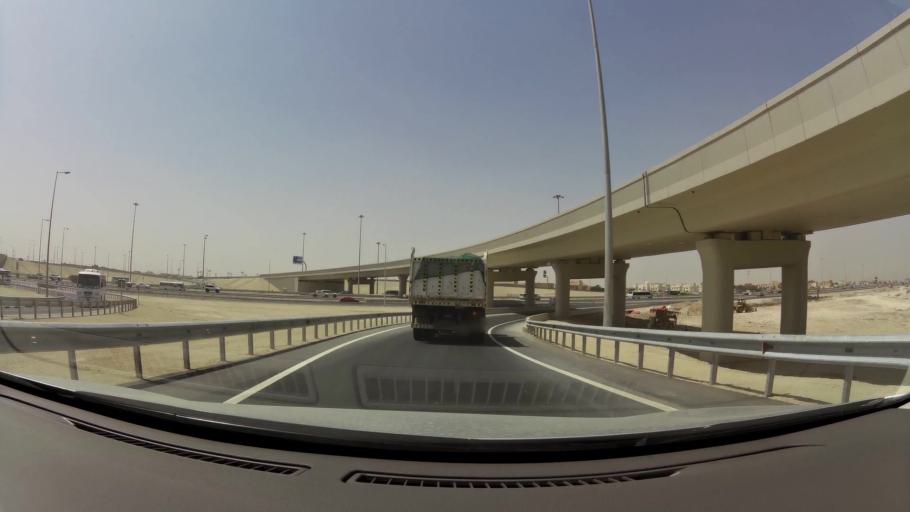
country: QA
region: Baladiyat Umm Salal
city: Umm Salal Muhammad
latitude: 25.3814
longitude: 51.4409
